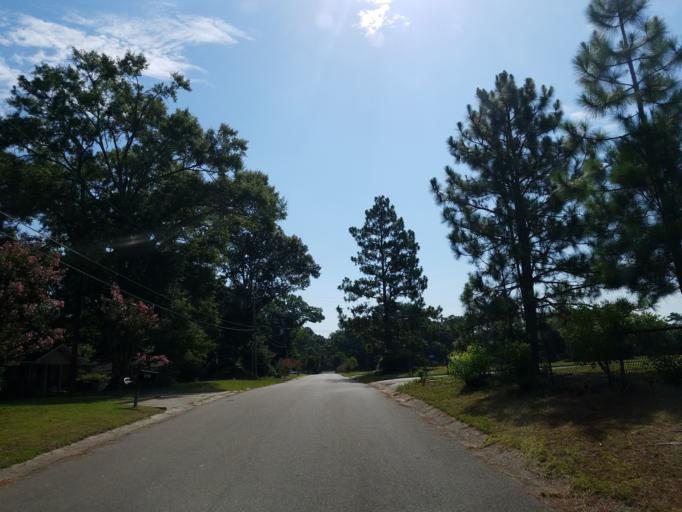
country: US
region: Mississippi
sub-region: Lamar County
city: West Hattiesburg
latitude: 31.3142
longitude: -89.3379
